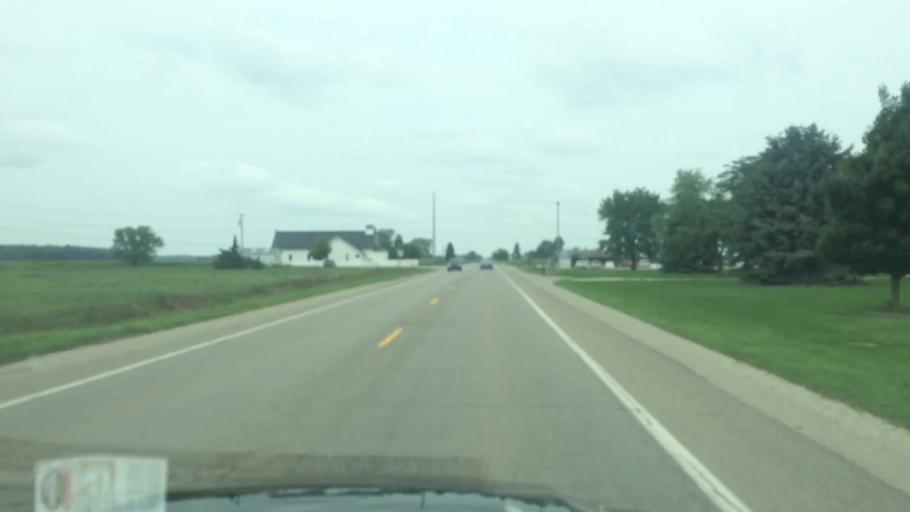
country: US
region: Michigan
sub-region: Huron County
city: Bad Axe
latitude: 43.8367
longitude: -83.0014
